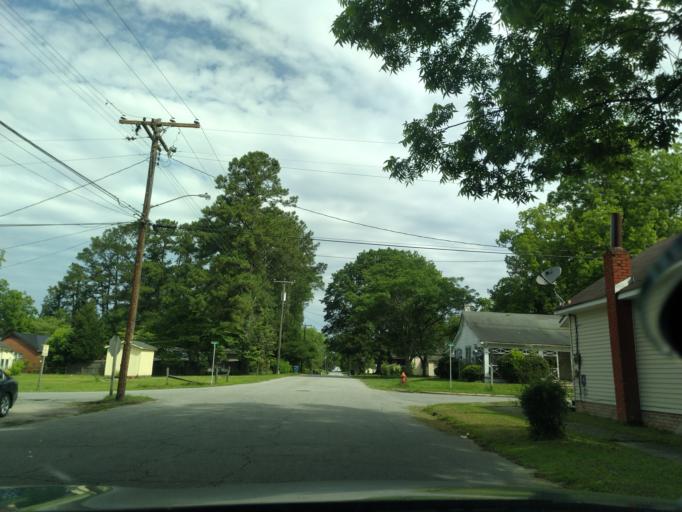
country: US
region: North Carolina
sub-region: Washington County
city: Plymouth
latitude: 35.8608
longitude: -76.7505
